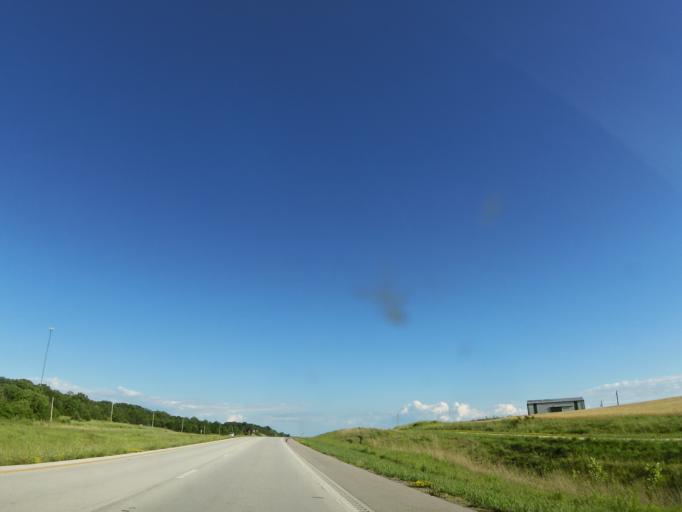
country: US
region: Missouri
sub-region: Pike County
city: Bowling Green
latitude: 39.4487
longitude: -91.2675
